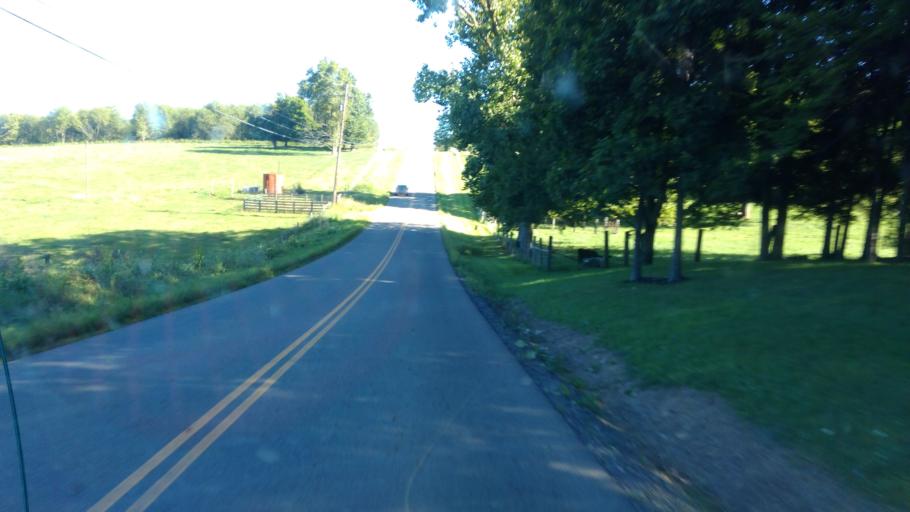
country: US
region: Ohio
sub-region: Knox County
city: Gambier
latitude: 40.4187
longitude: -82.3683
